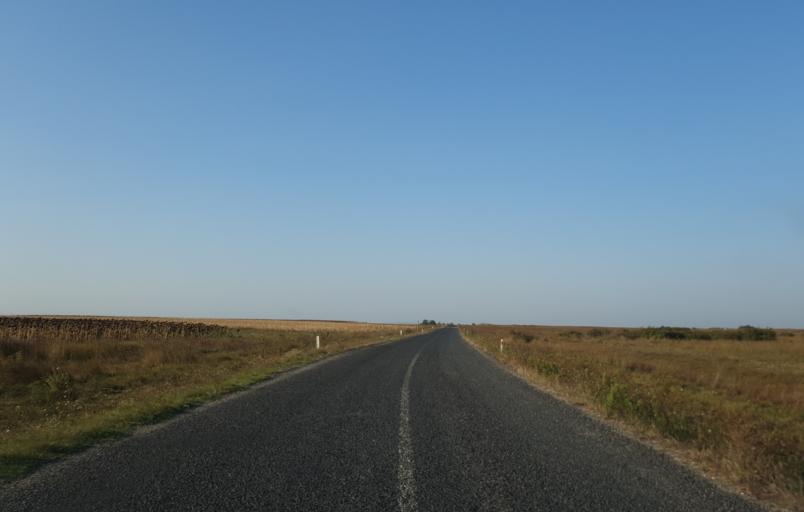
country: TR
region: Tekirdag
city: Beyazkoy
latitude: 41.4026
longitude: 27.7585
